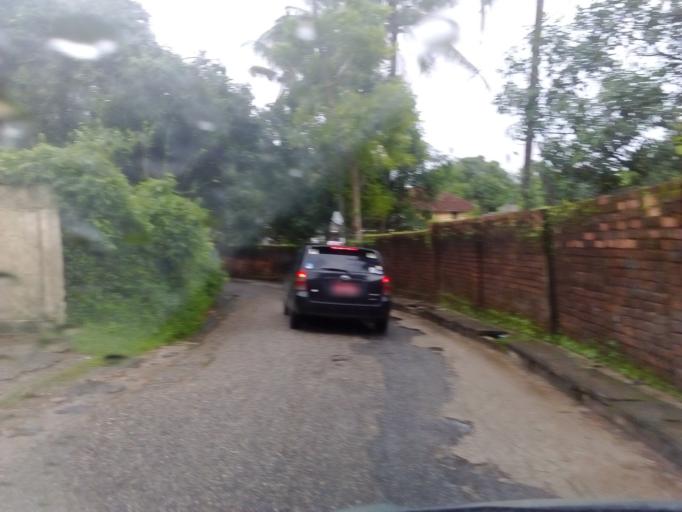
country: MM
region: Yangon
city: Yangon
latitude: 16.8221
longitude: 96.1513
